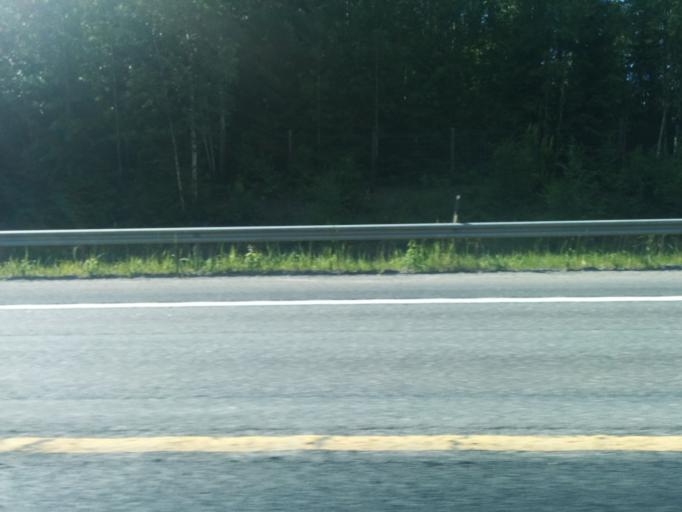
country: FI
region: Pirkanmaa
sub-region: Tampere
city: Tampere
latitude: 61.5188
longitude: 23.9200
